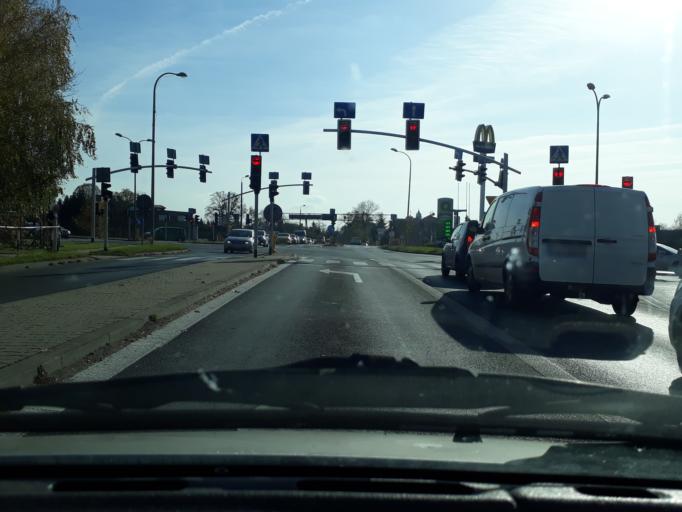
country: PL
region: Silesian Voivodeship
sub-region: Powiat tarnogorski
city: Tarnowskie Gory
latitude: 50.4319
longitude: 18.8660
